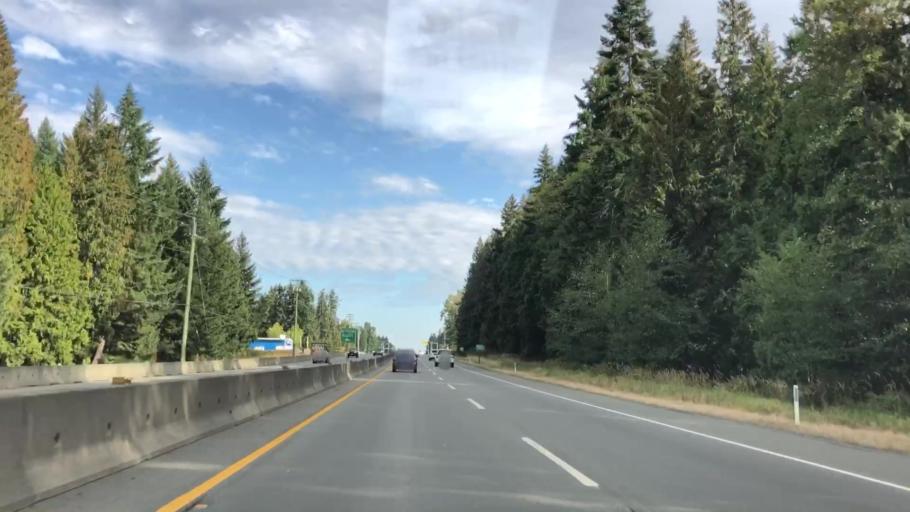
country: CA
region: British Columbia
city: Duncan
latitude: 48.6992
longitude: -123.5962
